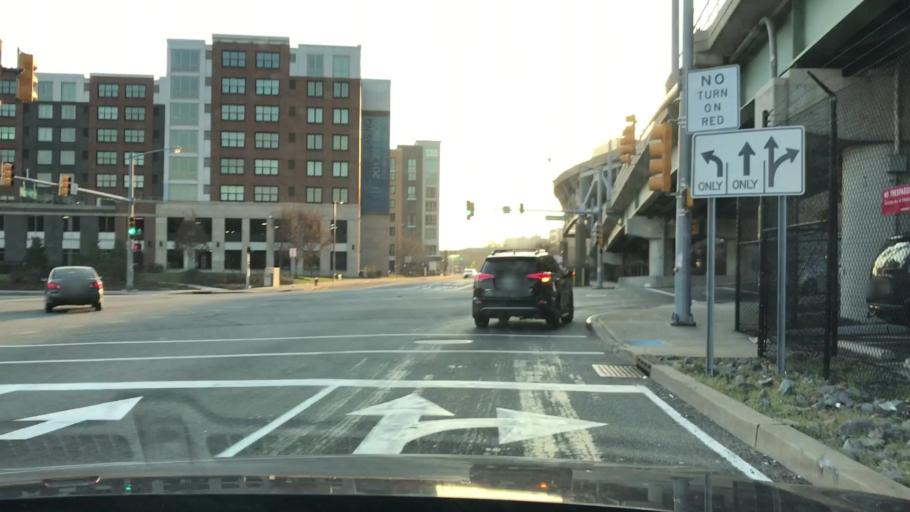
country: US
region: New Jersey
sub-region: Hudson County
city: Weehawken
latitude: 40.7640
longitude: -74.0206
